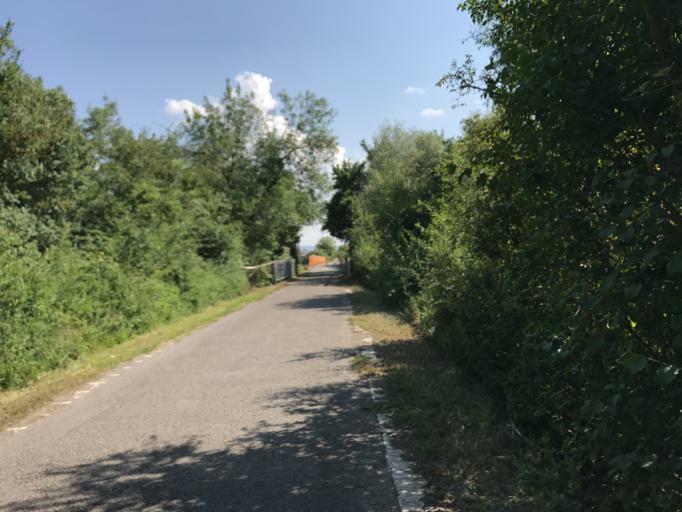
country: ES
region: Basque Country
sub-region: Provincia de Alava
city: Gasteiz / Vitoria
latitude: 42.8804
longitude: -2.6467
